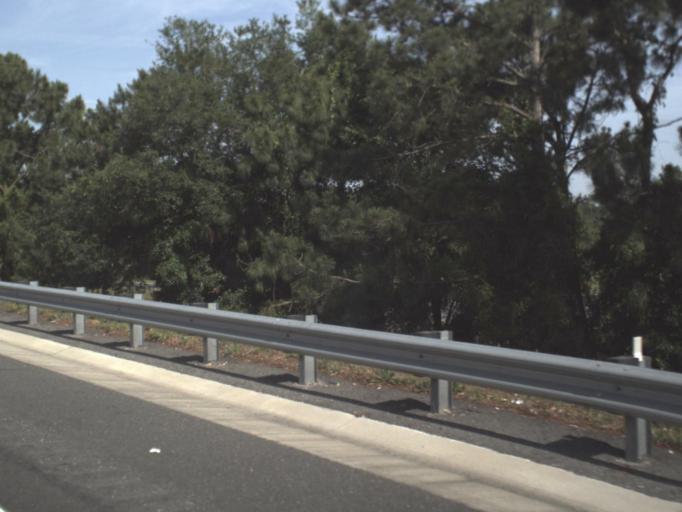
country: US
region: Florida
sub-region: Saint Johns County
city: Ponte Vedra Beach
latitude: 30.2517
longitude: -81.4657
